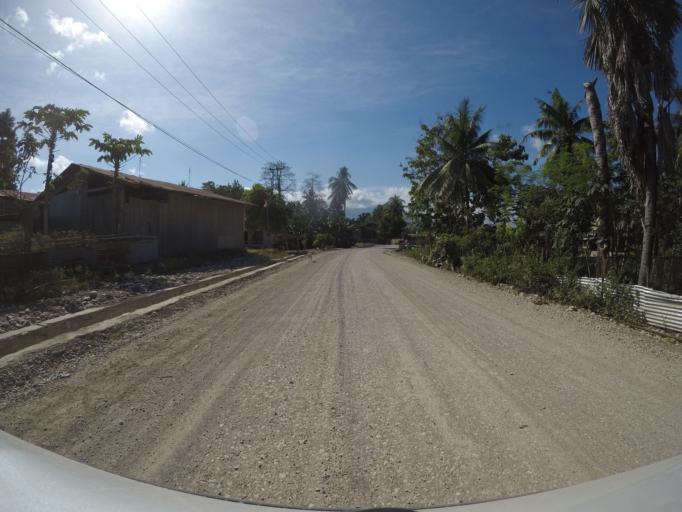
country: TL
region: Viqueque
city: Viqueque
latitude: -8.8472
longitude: 126.5122
